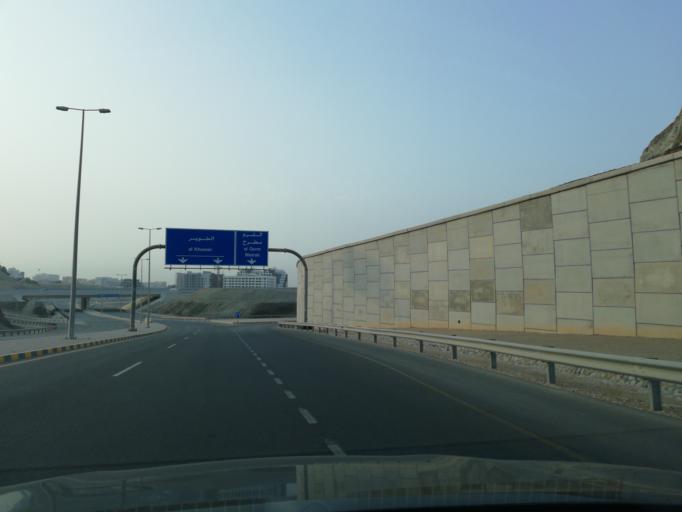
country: OM
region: Muhafazat Masqat
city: Bawshar
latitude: 23.5793
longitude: 58.4460
